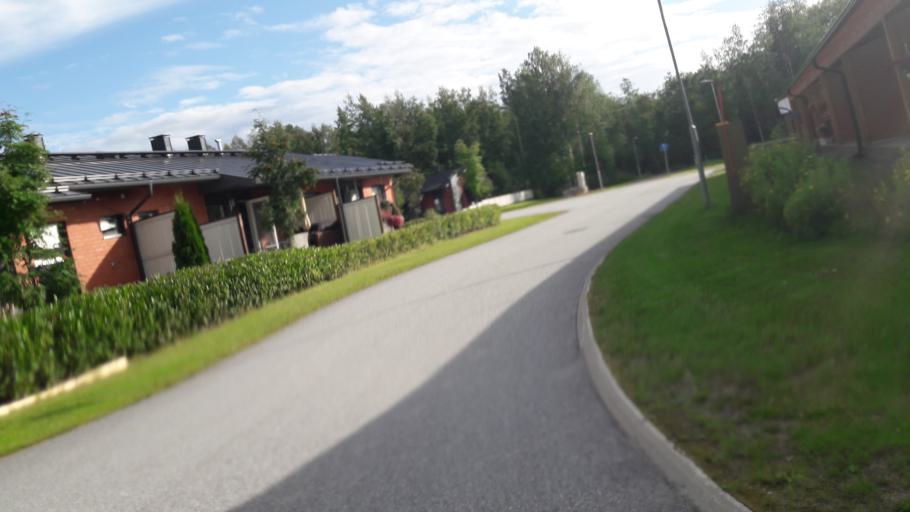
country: FI
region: North Karelia
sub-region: Joensuu
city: Joensuu
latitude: 62.5774
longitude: 29.7923
